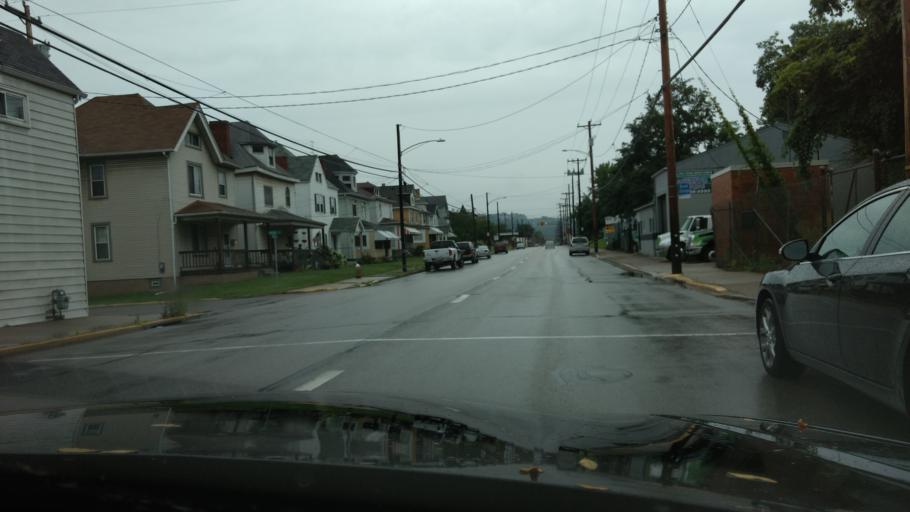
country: US
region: Pennsylvania
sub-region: Allegheny County
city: Coraopolis
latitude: 40.5154
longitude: -80.1558
